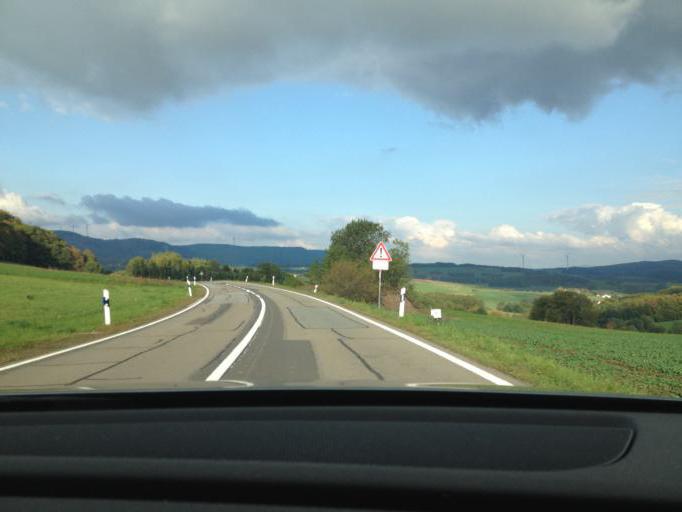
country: DE
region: Saarland
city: Freisen
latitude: 49.5091
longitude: 7.2431
